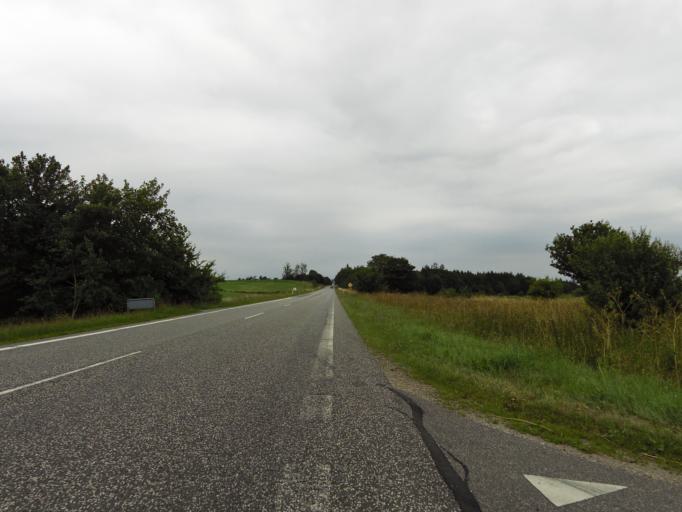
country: DK
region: South Denmark
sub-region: Tonder Kommune
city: Logumkloster
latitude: 55.1164
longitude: 8.9567
